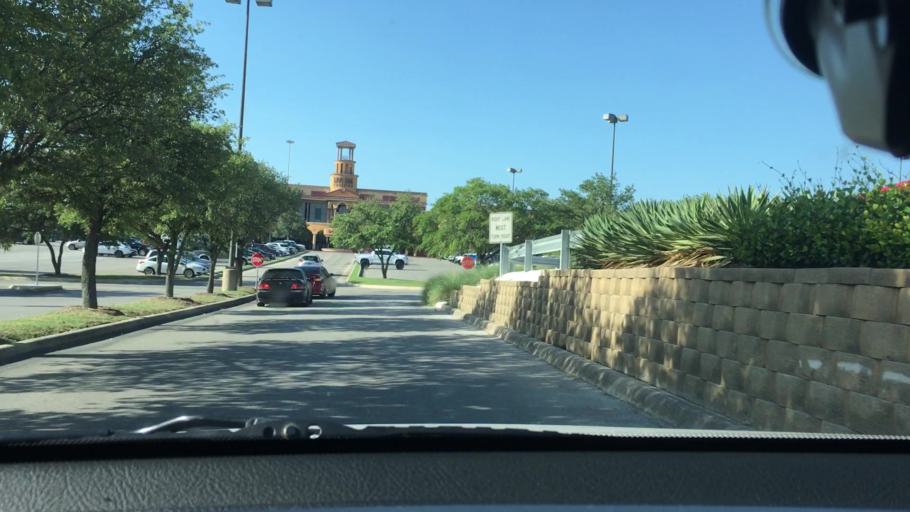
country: US
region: Texas
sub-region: Bexar County
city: Live Oak
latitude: 29.5635
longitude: -98.3335
